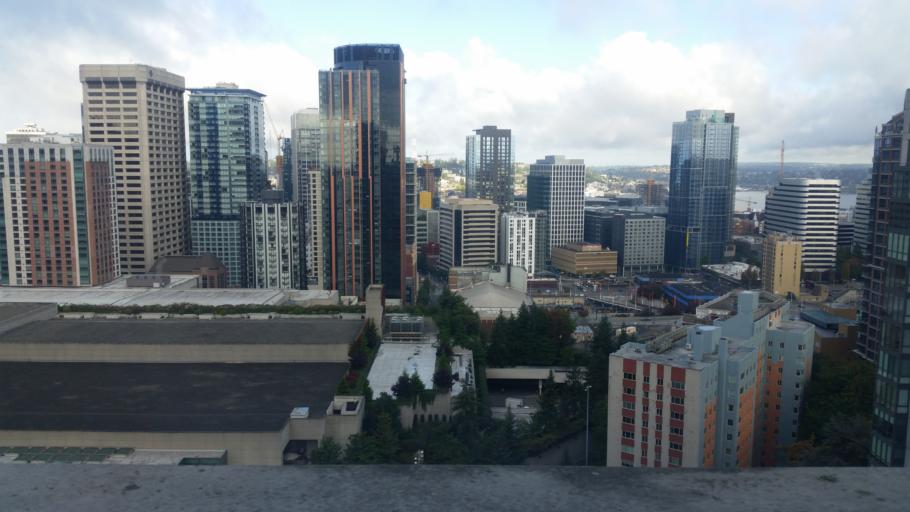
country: US
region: Washington
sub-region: King County
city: Seattle
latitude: 47.6108
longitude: -122.3293
